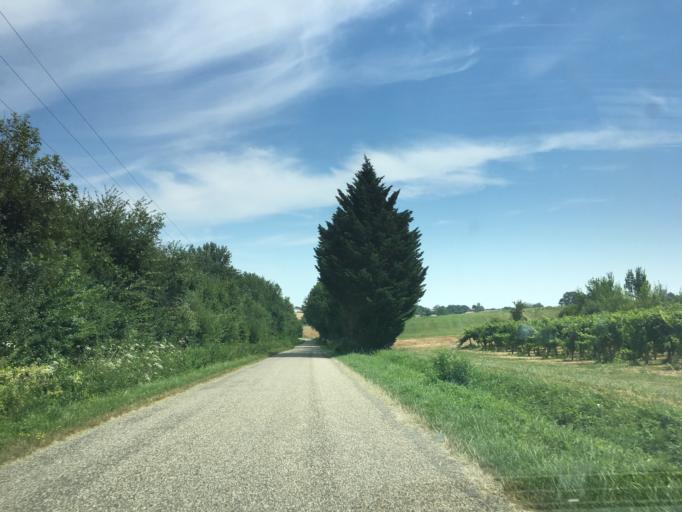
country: FR
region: Midi-Pyrenees
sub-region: Departement du Gers
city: Jegun
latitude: 43.8146
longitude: 0.5350
